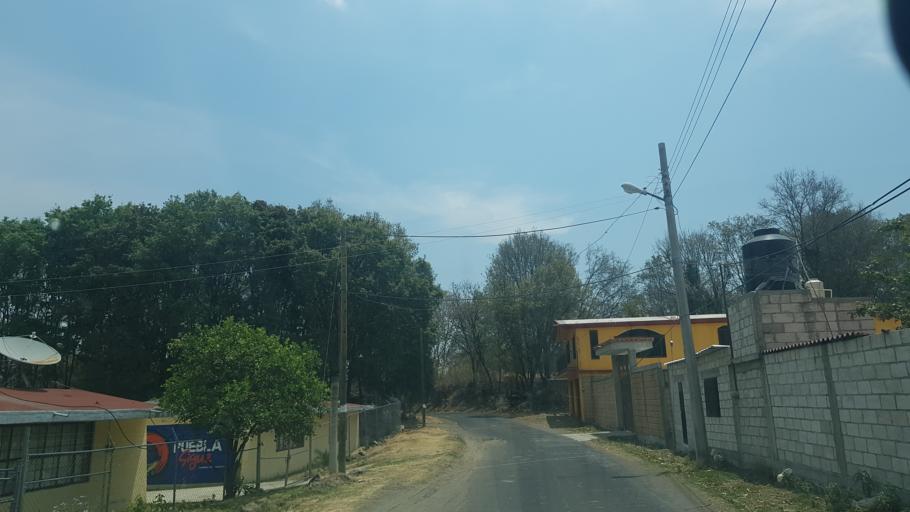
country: MX
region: Puebla
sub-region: Tochimilco
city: La Magdalena Yancuitlalpan
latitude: 18.8872
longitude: -98.6015
